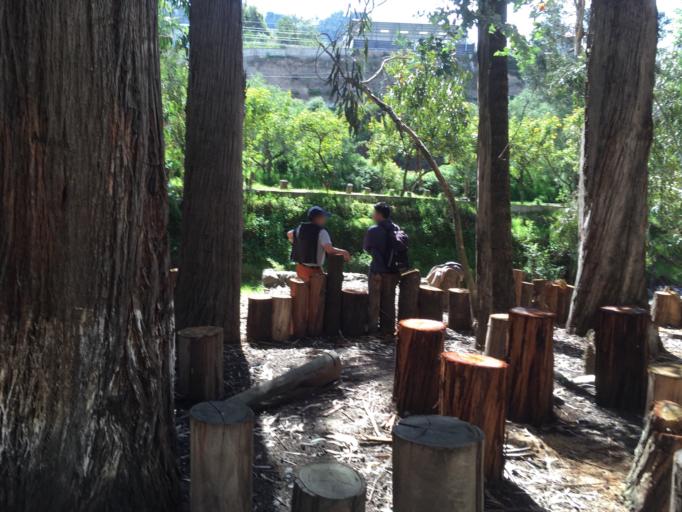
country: EC
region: Tungurahua
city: Ambato
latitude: -1.2493
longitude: -78.6400
